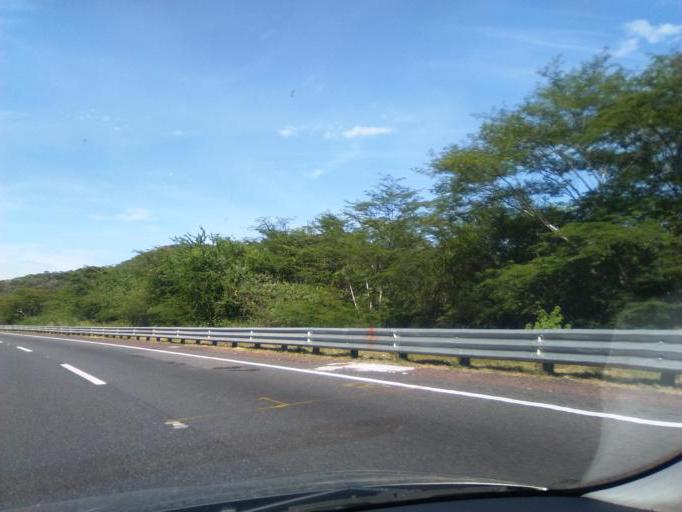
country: MX
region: Morelos
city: Tilzapotla
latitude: 18.3597
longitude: -99.1801
